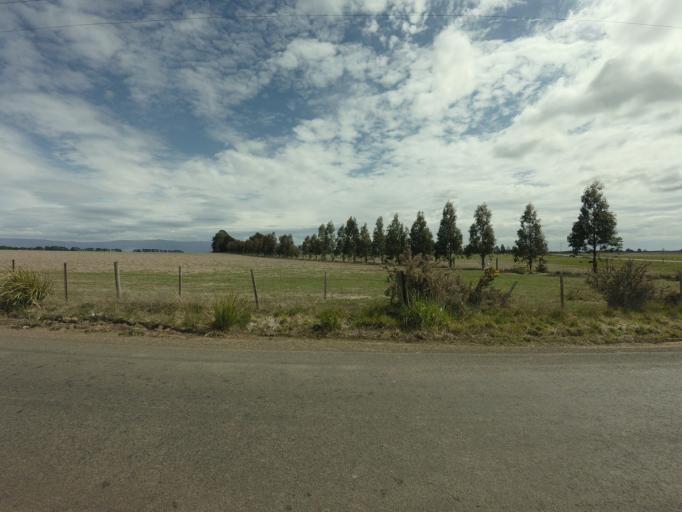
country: AU
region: Tasmania
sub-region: Northern Midlands
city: Longford
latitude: -41.7034
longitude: 147.1964
